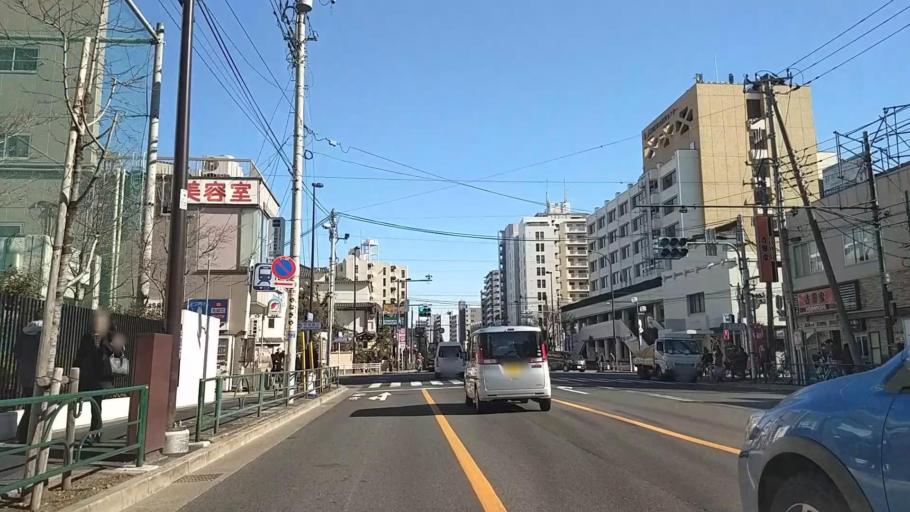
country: JP
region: Tokyo
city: Urayasu
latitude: 35.6894
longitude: 139.8260
